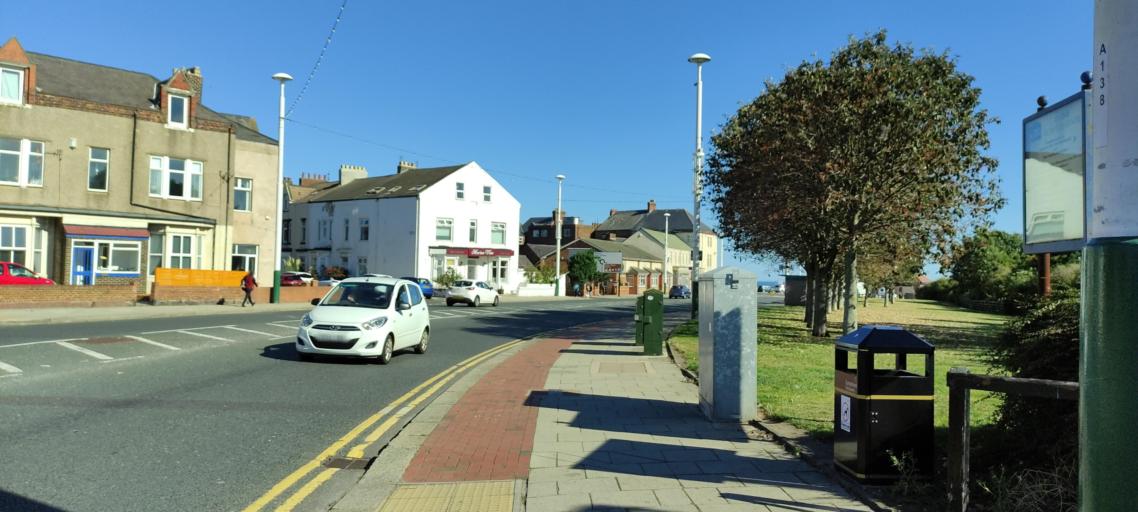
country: GB
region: England
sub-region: Sunderland
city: Sunderland
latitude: 54.9206
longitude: -1.3680
